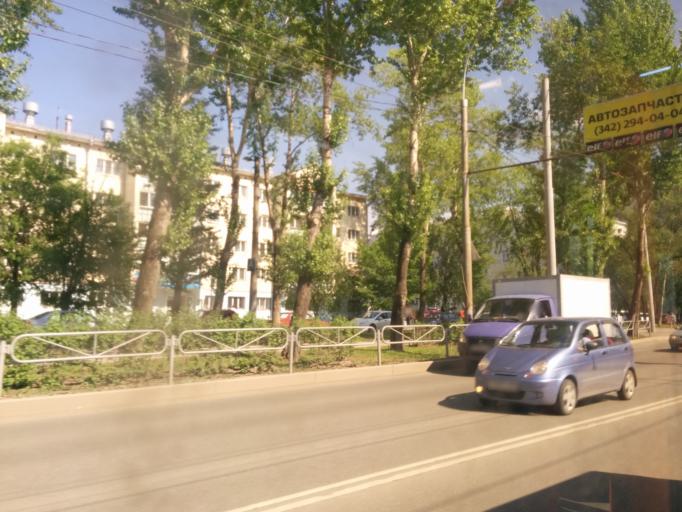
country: RU
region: Perm
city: Perm
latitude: 58.0113
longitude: 56.2801
